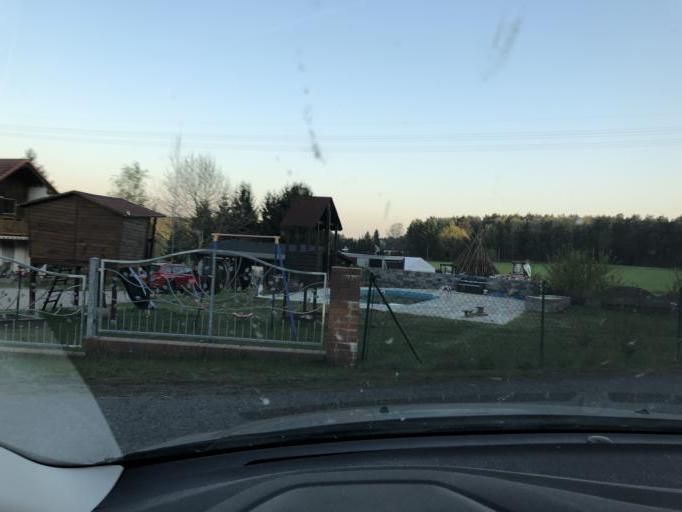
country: DE
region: Saxony
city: Gross Duben
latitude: 51.5784
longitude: 14.5494
